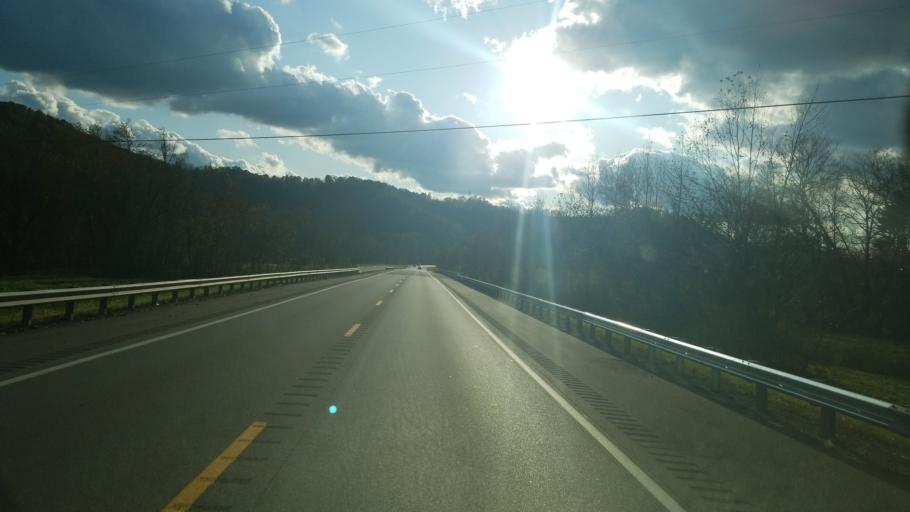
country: US
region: Kentucky
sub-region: Lewis County
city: Vanceburg
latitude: 38.5867
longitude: -83.3525
